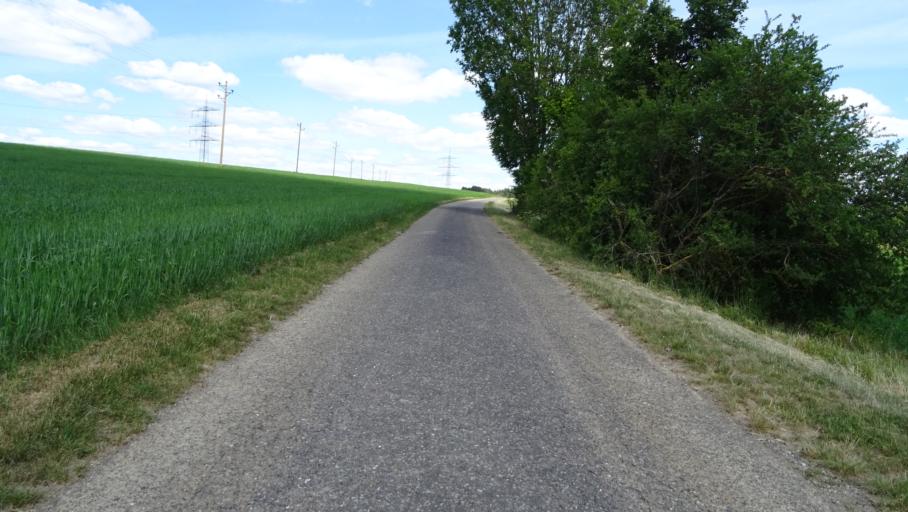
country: DE
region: Baden-Wuerttemberg
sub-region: Karlsruhe Region
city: Seckach
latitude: 49.4613
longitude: 9.3319
